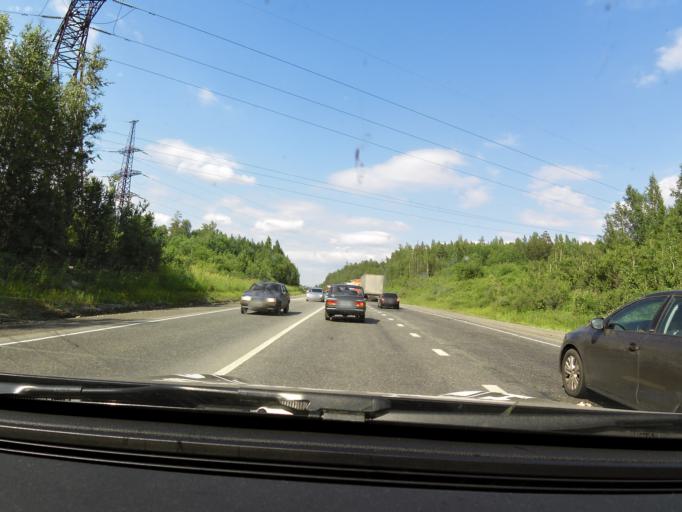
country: RU
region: Sverdlovsk
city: Talitsa
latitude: 56.8288
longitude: 59.9929
